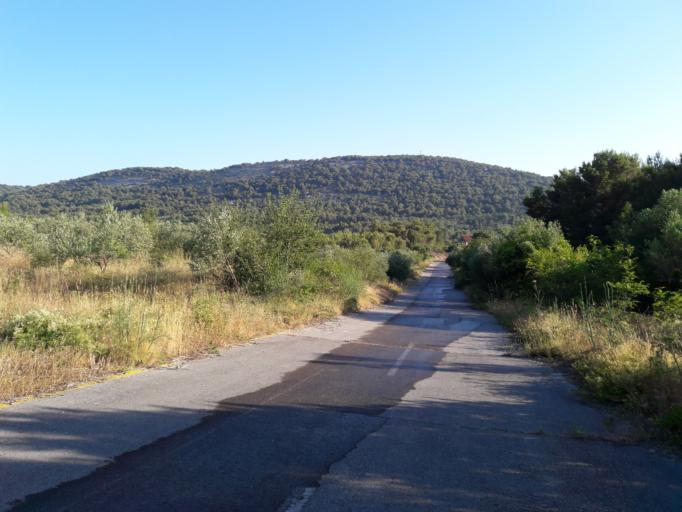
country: HR
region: Sibensko-Kniniska
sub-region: Grad Sibenik
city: Sibenik
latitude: 43.6970
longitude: 15.8469
